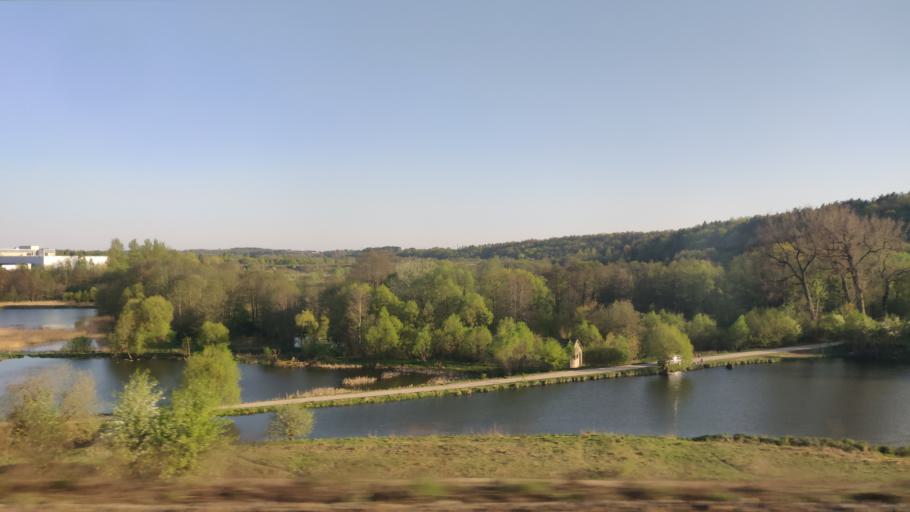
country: LT
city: Grigiskes
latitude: 54.6333
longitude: 25.1201
